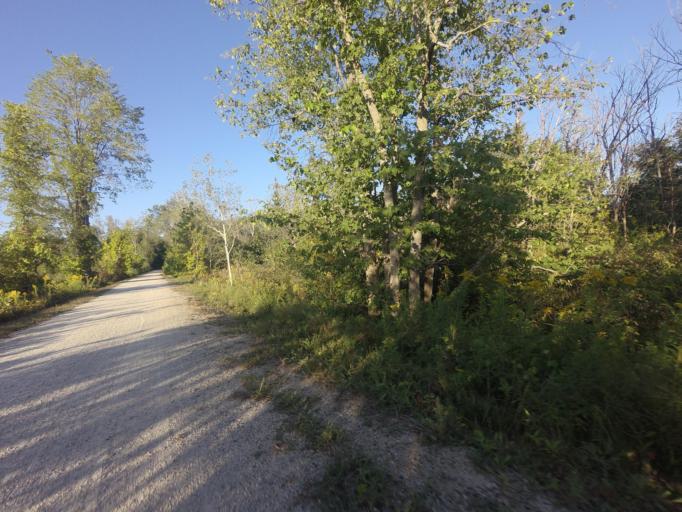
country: CA
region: Ontario
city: Brampton
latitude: 43.8280
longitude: -79.9099
